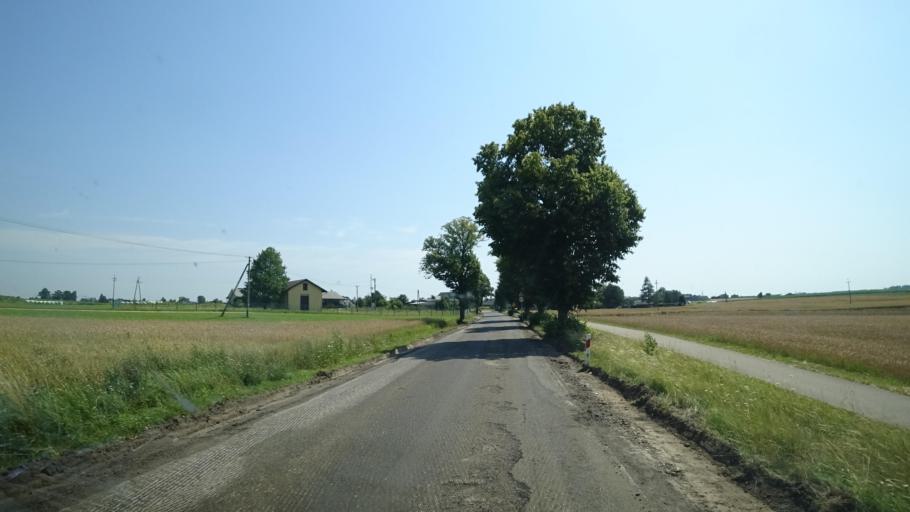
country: PL
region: Pomeranian Voivodeship
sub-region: Powiat chojnicki
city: Brusy
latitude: 53.8719
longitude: 17.6667
